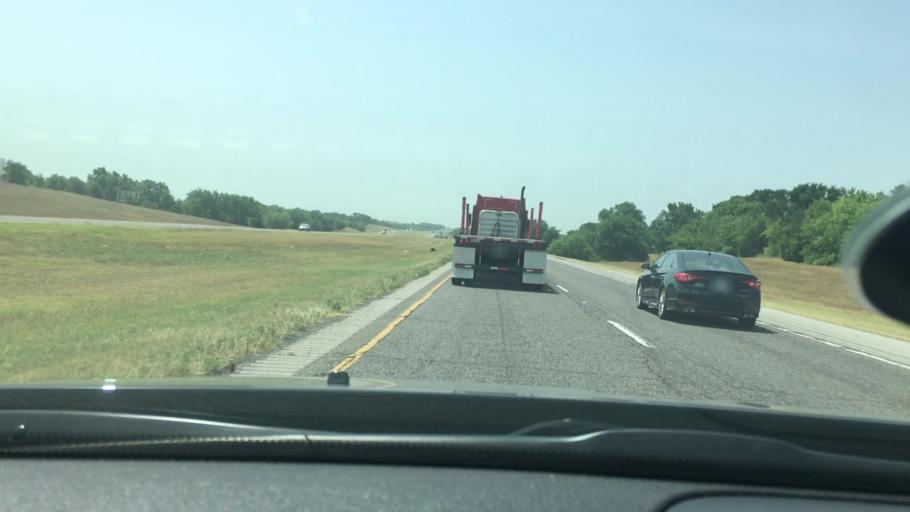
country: US
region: Oklahoma
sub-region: Garvin County
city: Wynnewood
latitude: 34.5987
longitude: -97.2101
